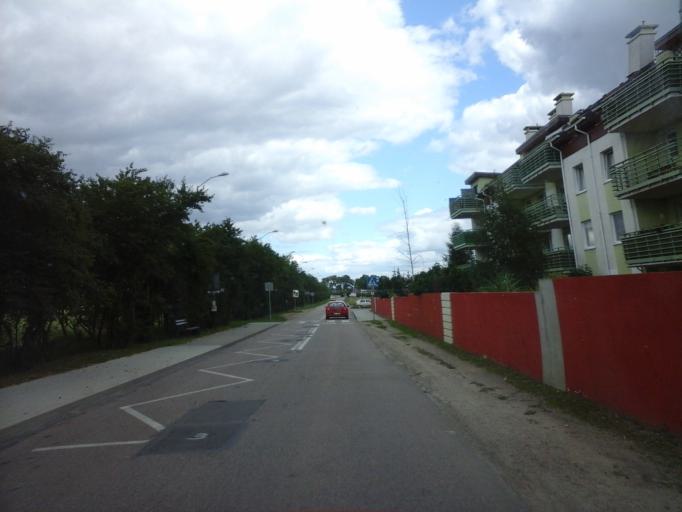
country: PL
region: West Pomeranian Voivodeship
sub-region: Powiat policki
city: Przeclaw
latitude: 53.3898
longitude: 14.4757
